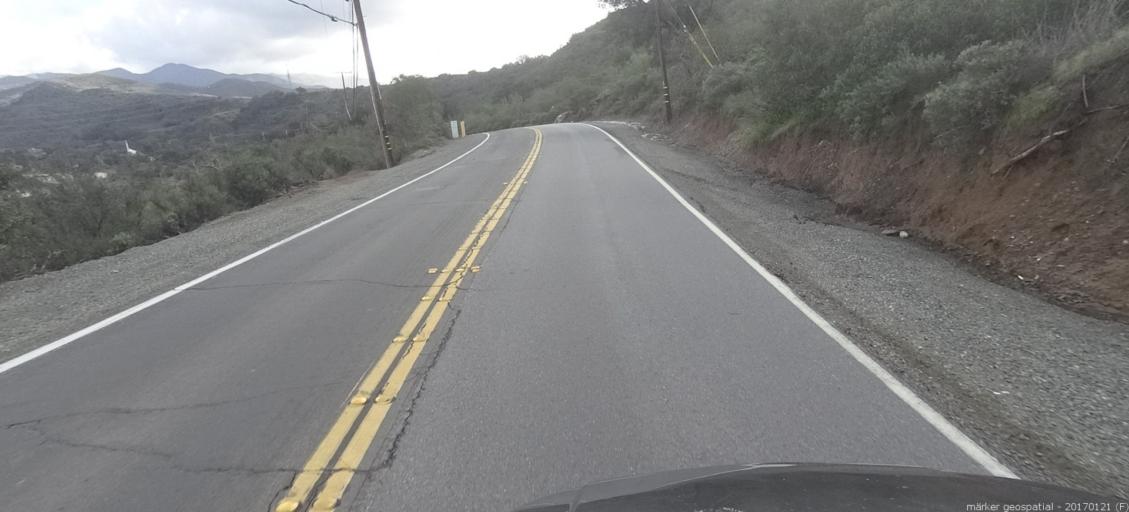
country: US
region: California
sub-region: Orange County
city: Foothill Ranch
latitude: 33.7455
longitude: -117.6644
